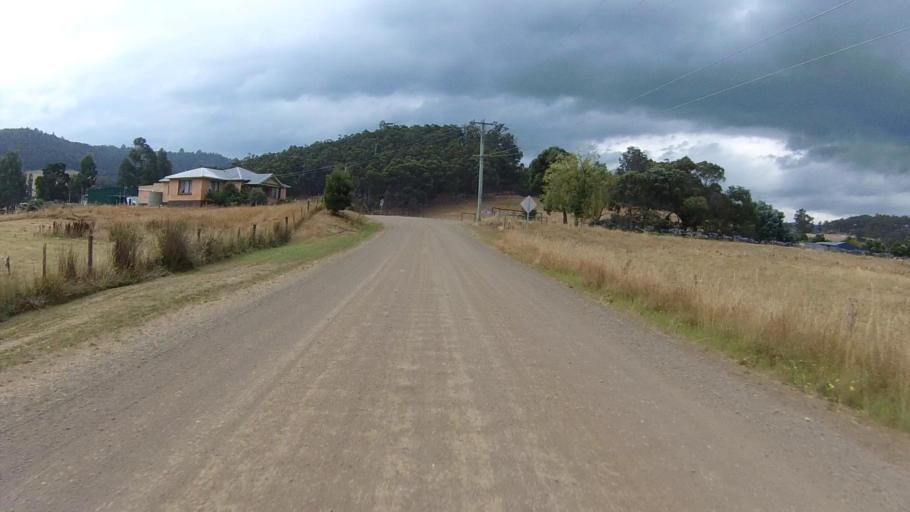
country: AU
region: Tasmania
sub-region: Huon Valley
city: Huonville
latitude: -42.9787
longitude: 147.0548
